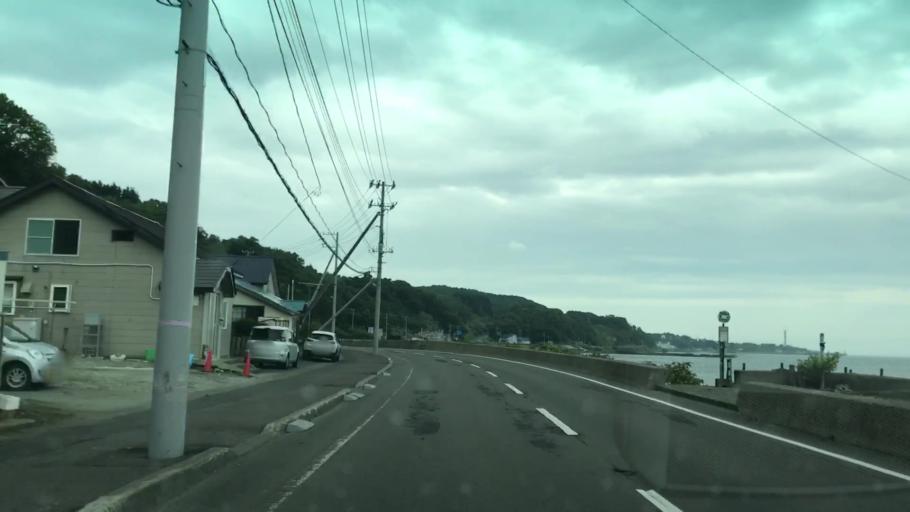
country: JP
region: Hokkaido
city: Iwanai
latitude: 42.7716
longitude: 140.2433
